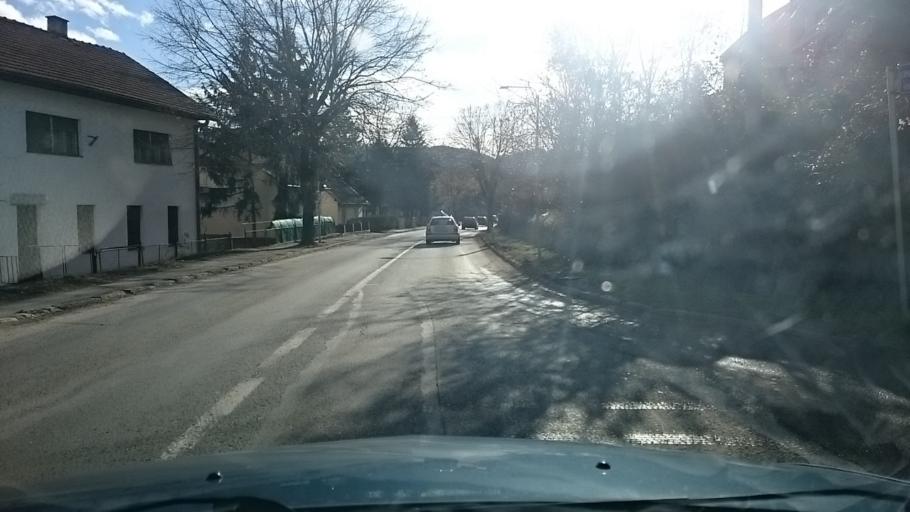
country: BA
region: Republika Srpska
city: Banja Luka
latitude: 44.7693
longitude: 17.1814
